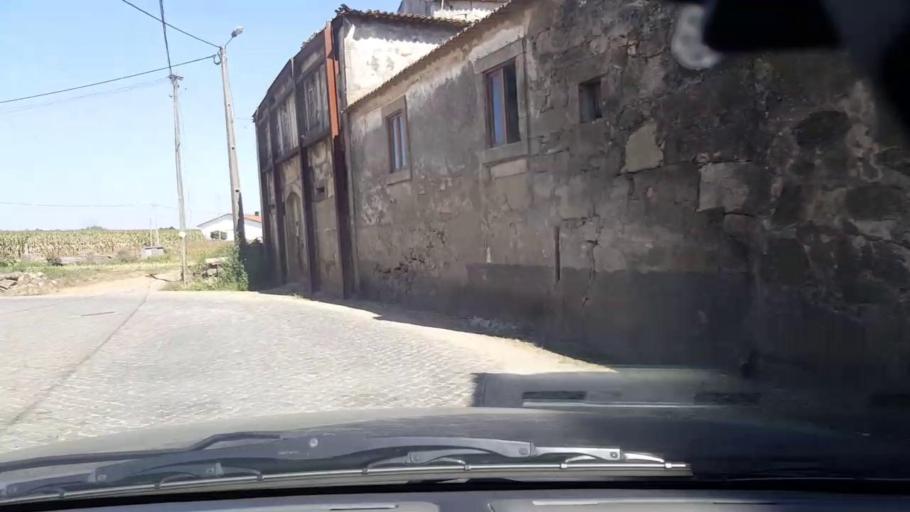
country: PT
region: Porto
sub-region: Matosinhos
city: Lavra
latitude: 41.2760
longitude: -8.7087
